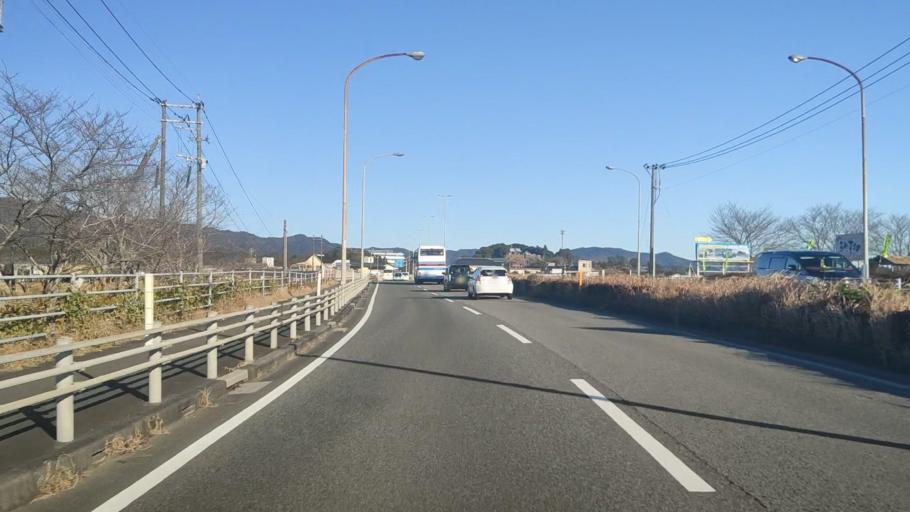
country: JP
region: Miyazaki
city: Nobeoka
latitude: 32.4632
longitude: 131.6488
